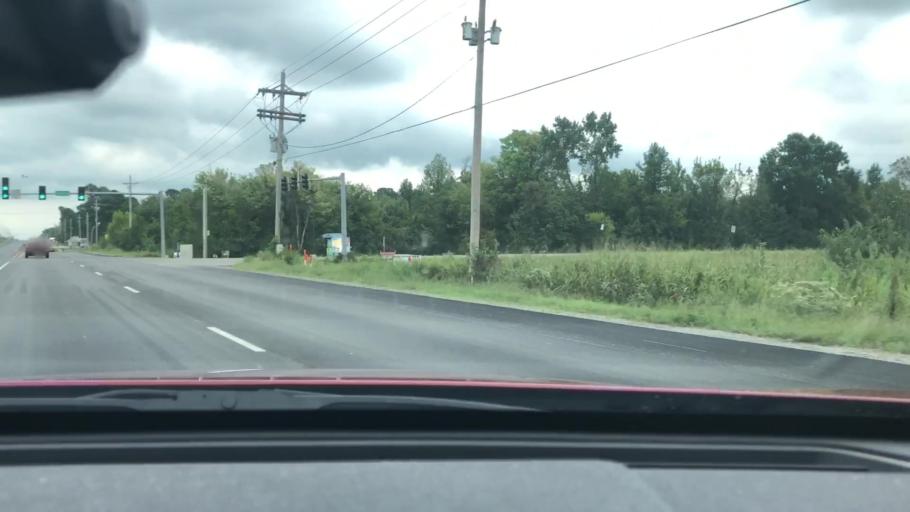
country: US
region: Arkansas
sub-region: Miller County
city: Texarkana
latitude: 33.4305
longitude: -94.0005
